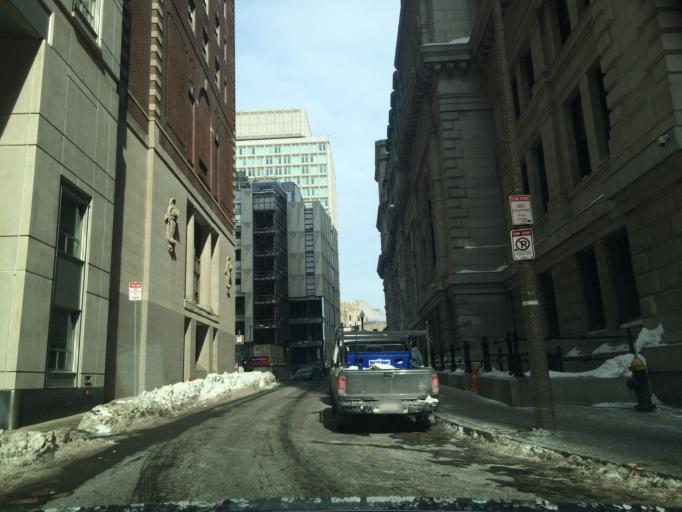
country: US
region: Massachusetts
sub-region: Suffolk County
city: Boston
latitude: 42.3586
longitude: -71.0615
